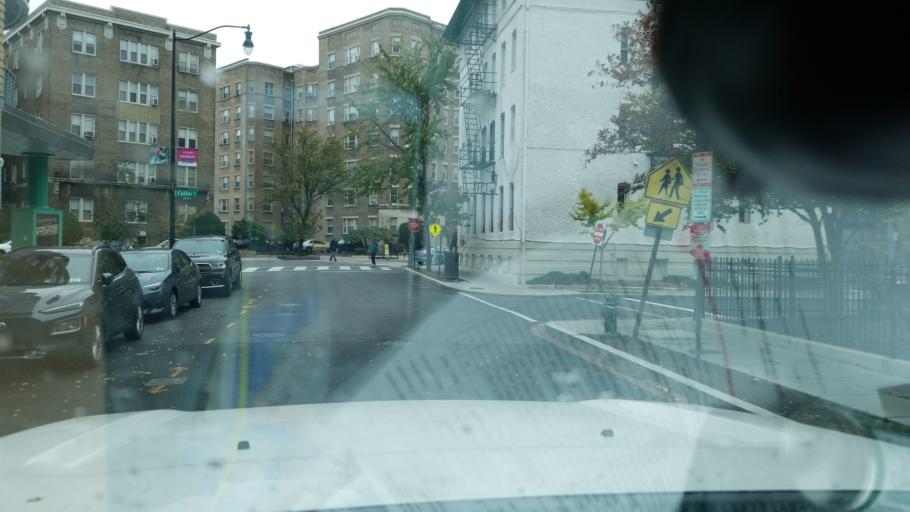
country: US
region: Washington, D.C.
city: Washington, D.C.
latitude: 38.9234
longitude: -77.0390
